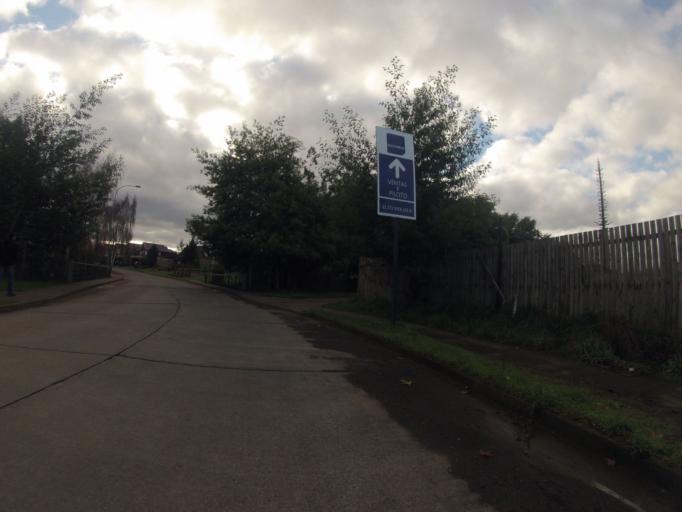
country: CL
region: Araucania
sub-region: Provincia de Cautin
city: Temuco
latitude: -38.7347
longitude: -72.6451
